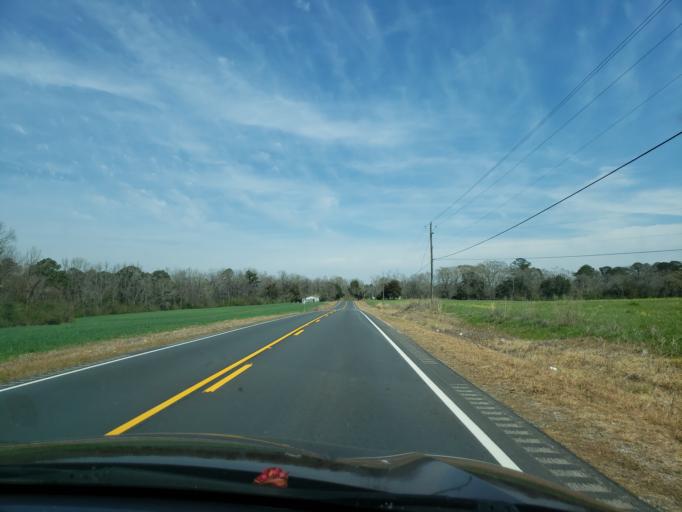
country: US
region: Alabama
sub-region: Elmore County
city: Tallassee
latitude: 32.5607
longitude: -85.7885
